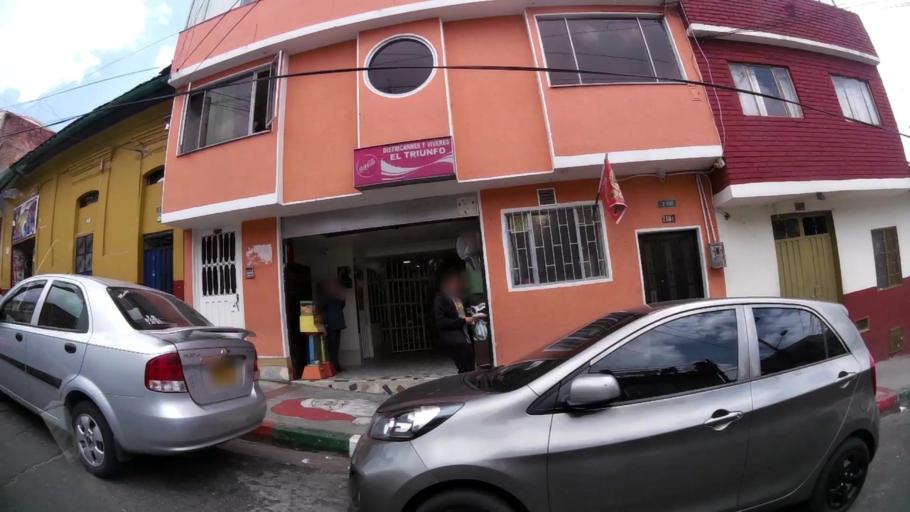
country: CO
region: Bogota D.C.
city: Bogota
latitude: 4.5909
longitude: -74.0715
